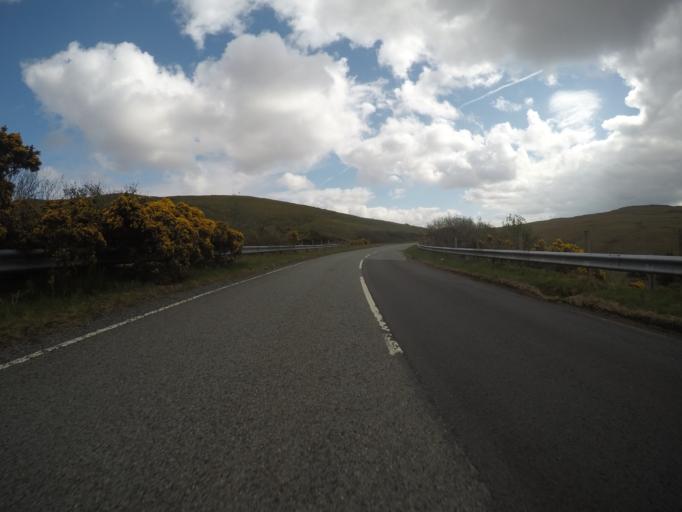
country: GB
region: Scotland
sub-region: Highland
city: Isle of Skye
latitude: 57.3287
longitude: -6.3341
